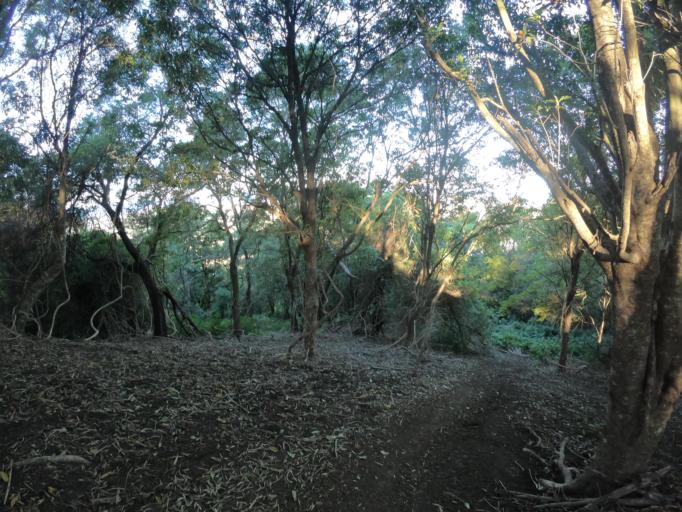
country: AU
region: New South Wales
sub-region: Wollongong
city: Mount Keira
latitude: -34.4206
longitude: 150.8401
